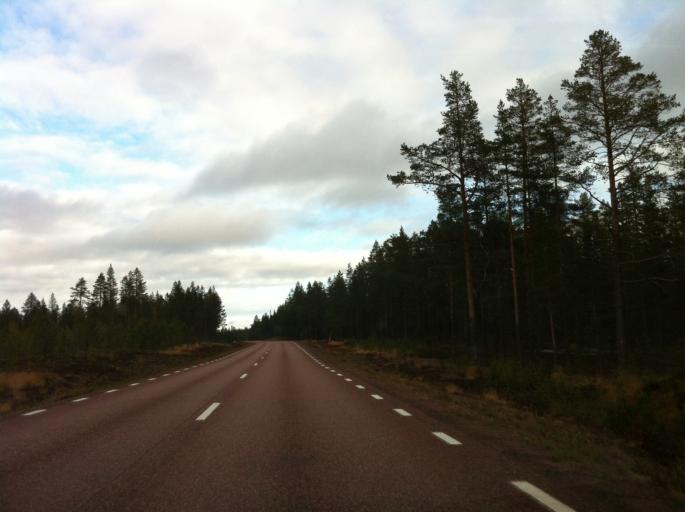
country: SE
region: Dalarna
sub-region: Alvdalens Kommun
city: AElvdalen
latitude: 61.4774
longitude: 13.4229
